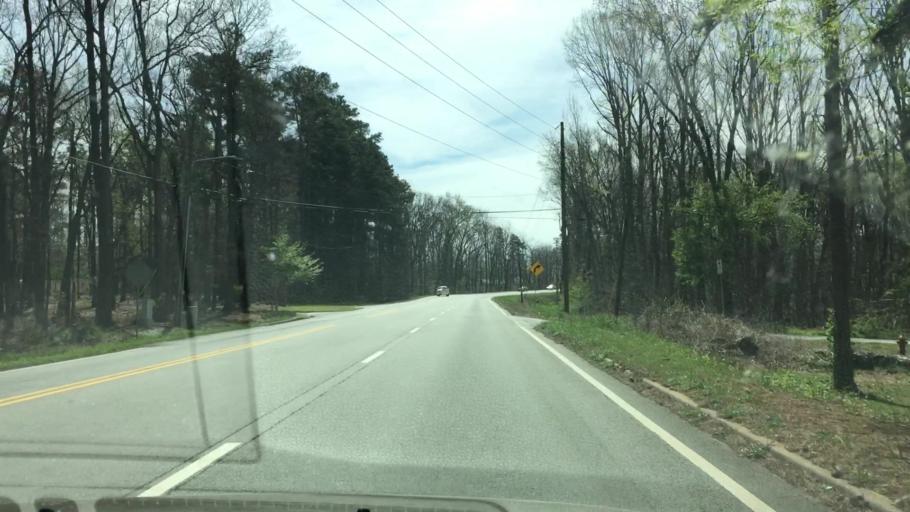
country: US
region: Georgia
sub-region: Barrow County
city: Winder
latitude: 34.0184
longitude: -83.7090
